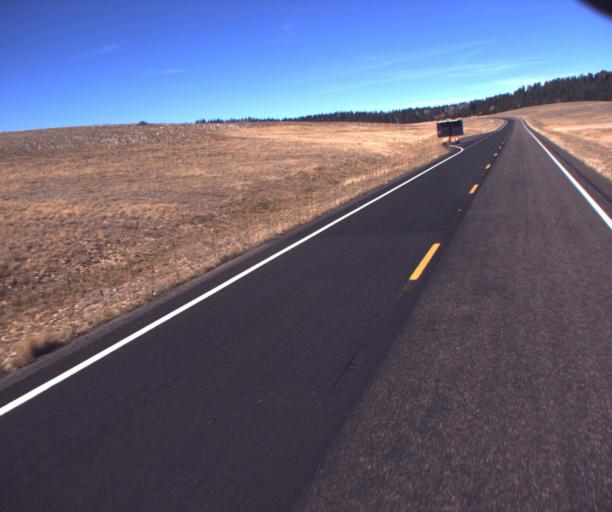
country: US
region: Arizona
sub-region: Coconino County
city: Grand Canyon
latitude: 36.4921
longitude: -112.1311
